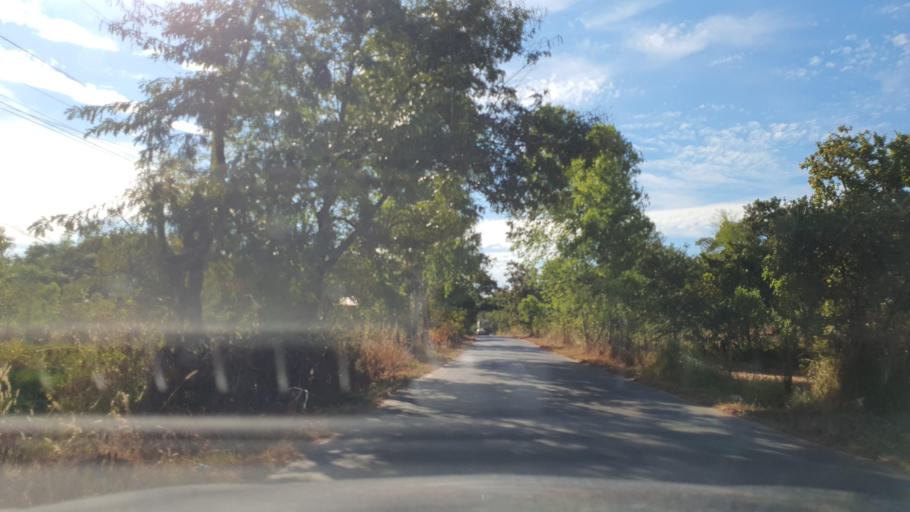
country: TH
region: Kalasin
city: Kuchinarai
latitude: 16.5413
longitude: 104.0838
